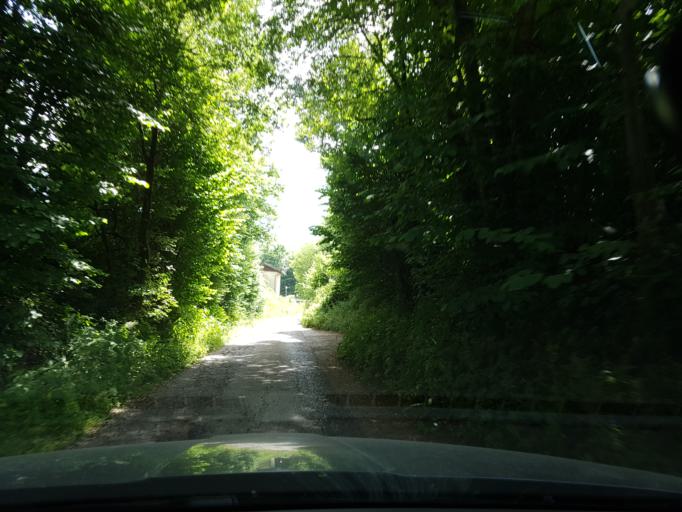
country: AT
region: Carinthia
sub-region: Politischer Bezirk Spittal an der Drau
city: Millstatt
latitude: 46.7751
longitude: 13.5523
